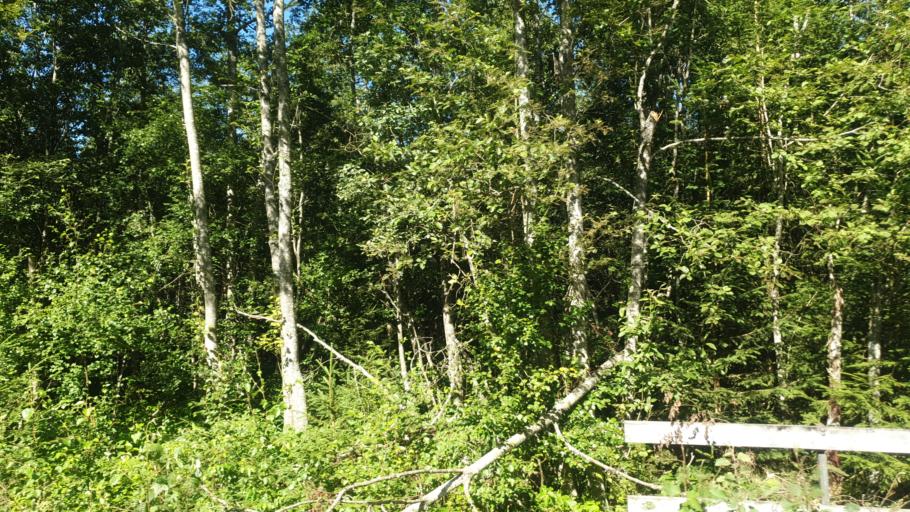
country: NO
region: Sor-Trondelag
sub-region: Orkdal
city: Orkanger
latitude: 63.1856
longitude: 9.7737
